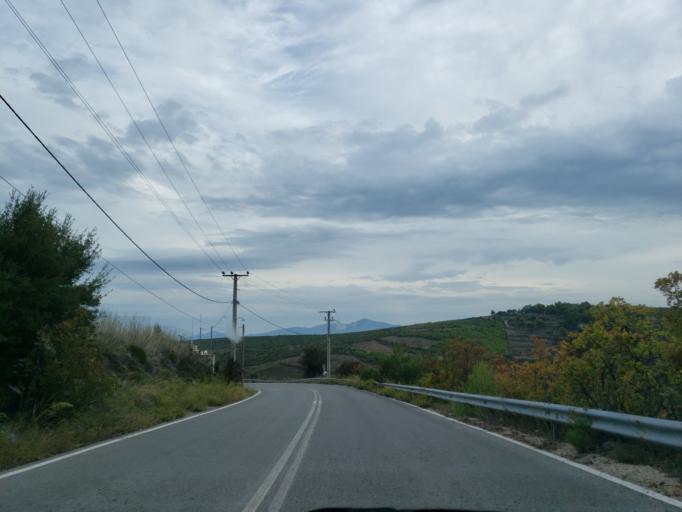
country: GR
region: Attica
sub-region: Nomarchia Anatolikis Attikis
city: Varnavas
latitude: 38.2138
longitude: 23.9400
